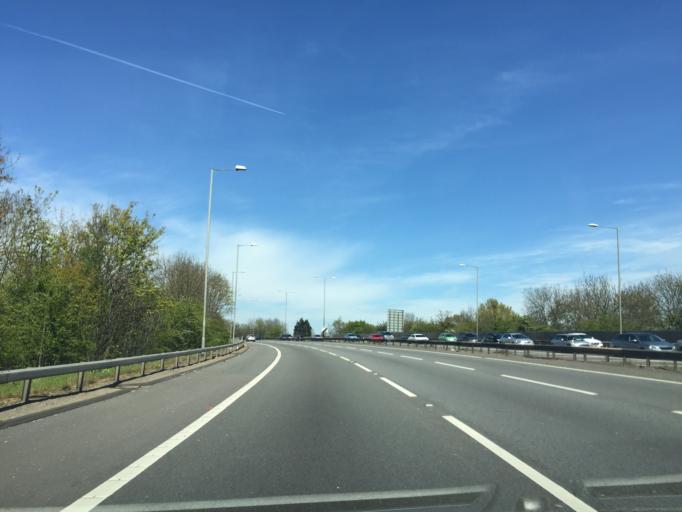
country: GB
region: England
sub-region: Greater London
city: Woodford Green
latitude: 51.6033
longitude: 0.0488
